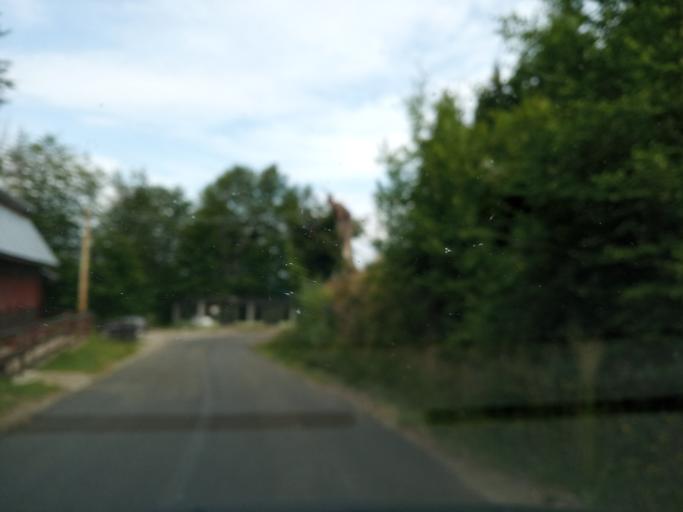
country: RO
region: Hunedoara
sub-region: Oras Petrila
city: Petrila
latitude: 45.3915
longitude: 23.4368
